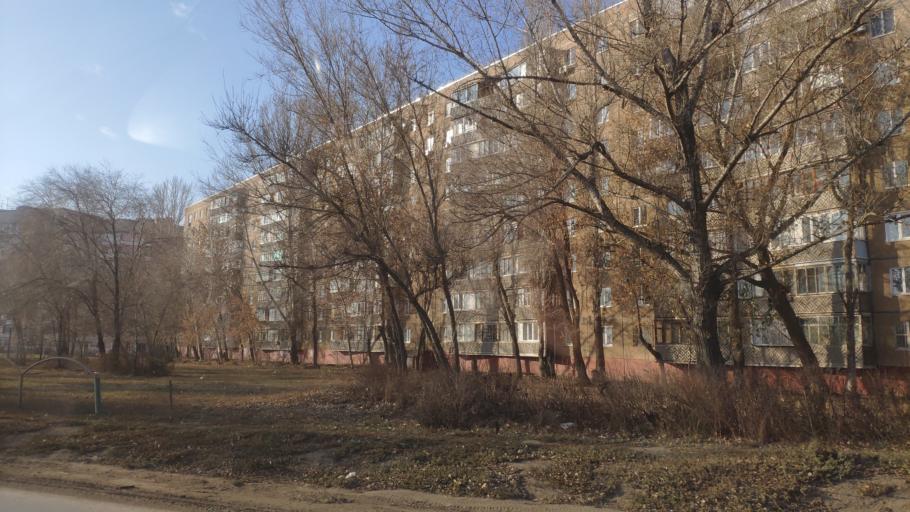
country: RU
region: Orenburg
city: Prigorodnyy
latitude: 51.7766
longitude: 55.1919
